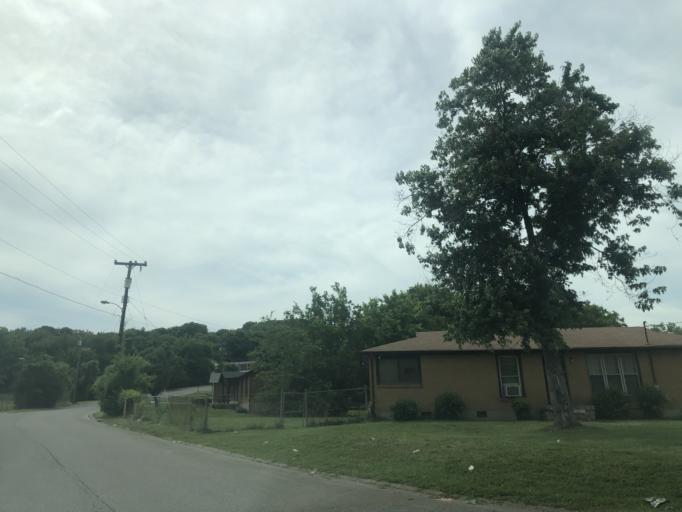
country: US
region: Tennessee
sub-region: Davidson County
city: Nashville
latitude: 36.2217
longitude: -86.8252
